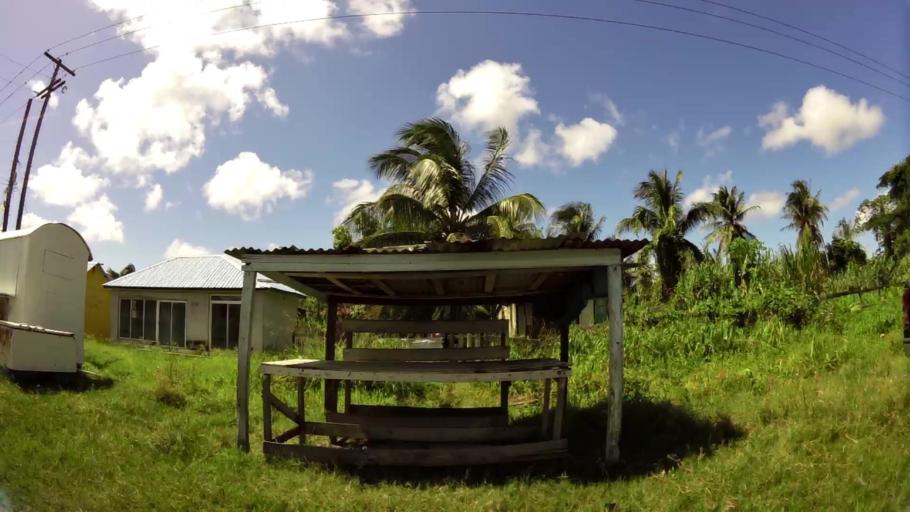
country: GY
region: Demerara-Mahaica
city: Georgetown
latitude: 6.7824
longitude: -58.1259
